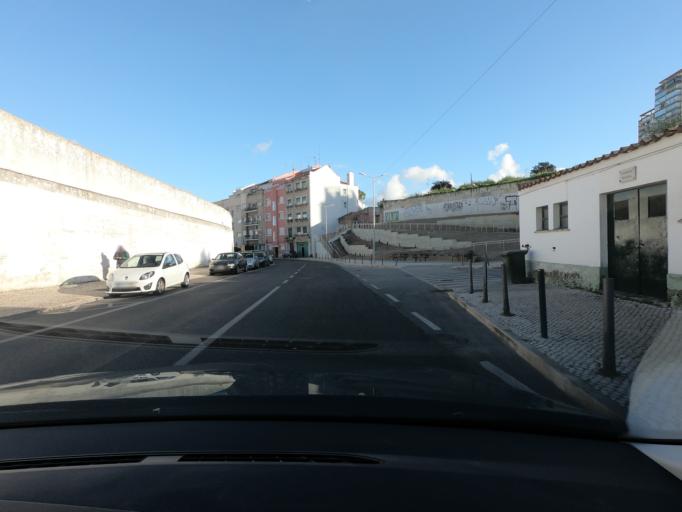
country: PT
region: Lisbon
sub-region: Lisbon
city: Lisbon
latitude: 38.7270
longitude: -9.1145
